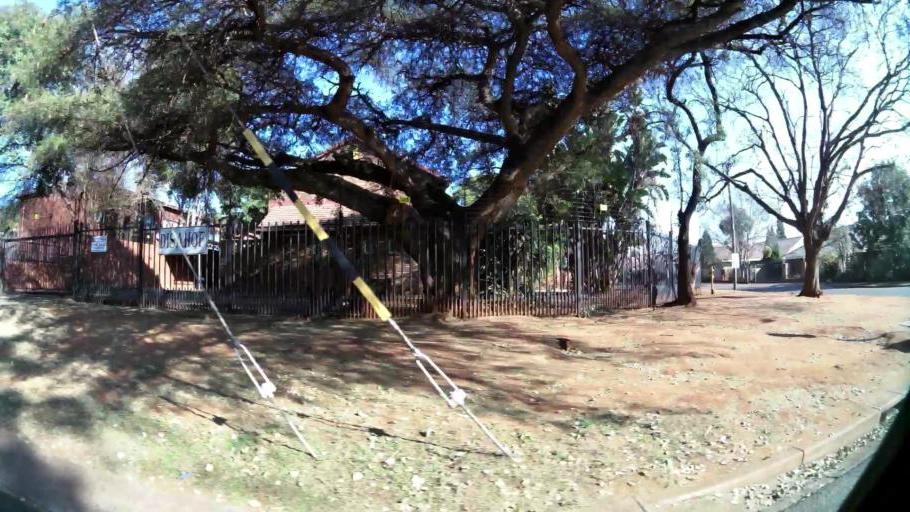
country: ZA
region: Gauteng
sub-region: City of Tshwane Metropolitan Municipality
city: Pretoria
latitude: -25.6706
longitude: 28.1556
